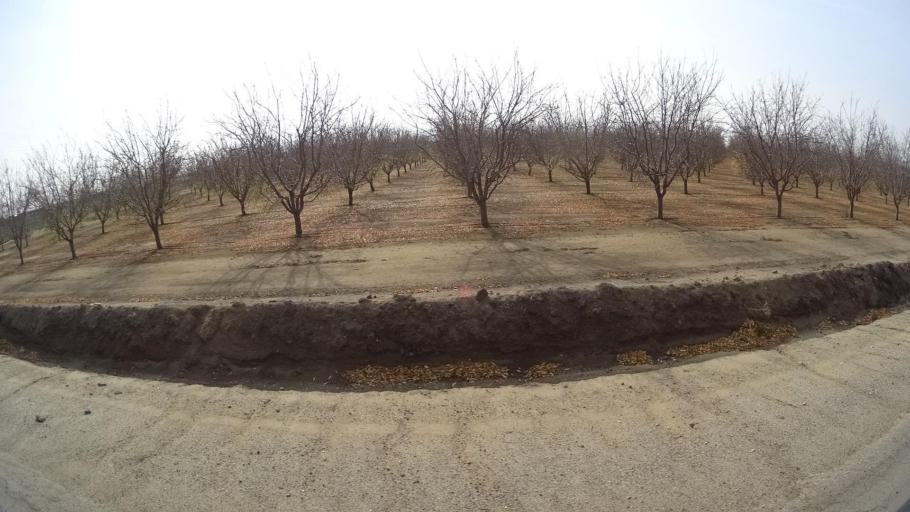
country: US
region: California
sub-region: Kern County
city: Greenfield
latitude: 35.0764
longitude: -119.0322
